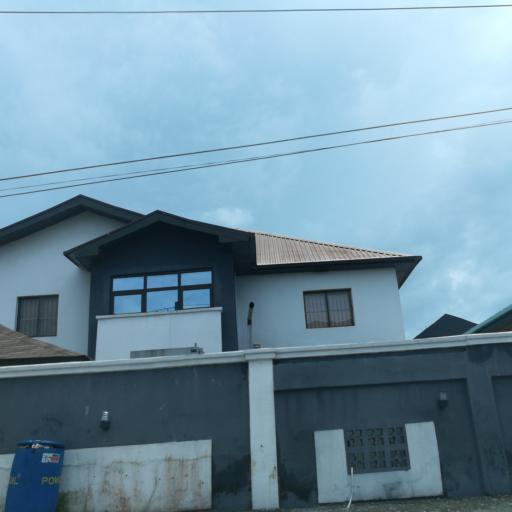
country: NG
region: Lagos
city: Ikoyi
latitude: 6.4402
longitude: 3.4668
